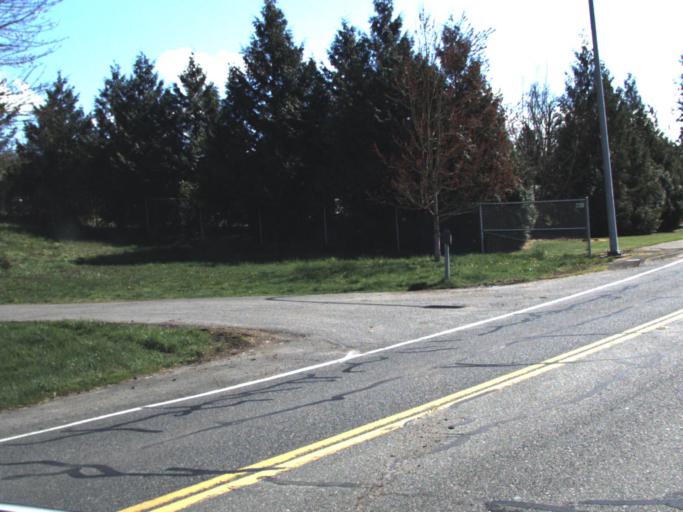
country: US
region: Washington
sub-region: King County
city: Enumclaw
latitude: 47.2248
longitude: -121.9897
